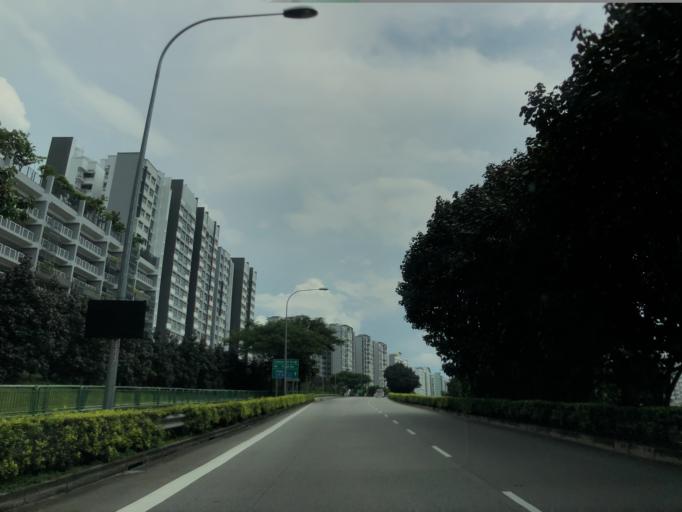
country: MY
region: Johor
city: Kampung Pasir Gudang Baru
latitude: 1.4006
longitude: 103.8936
